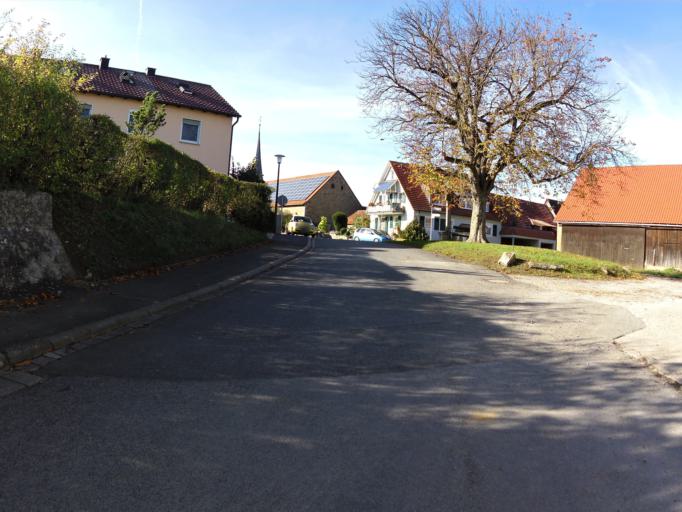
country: DE
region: Bavaria
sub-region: Regierungsbezirk Unterfranken
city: Biebelried
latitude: 49.7282
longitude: 10.0903
